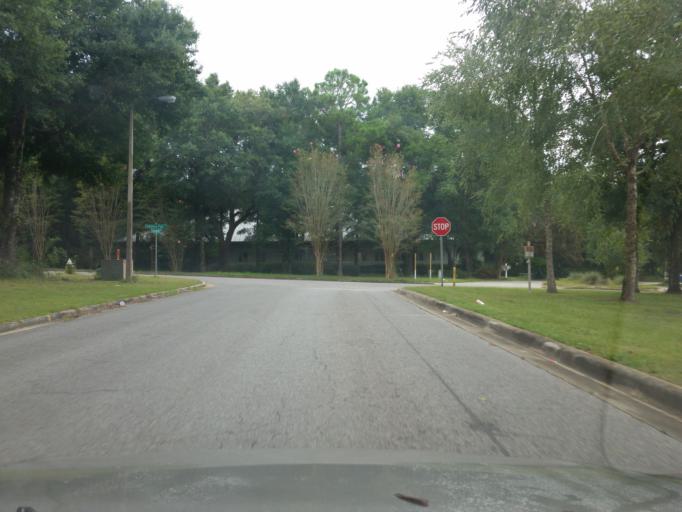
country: US
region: Florida
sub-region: Escambia County
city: Brent
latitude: 30.4781
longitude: -87.2662
